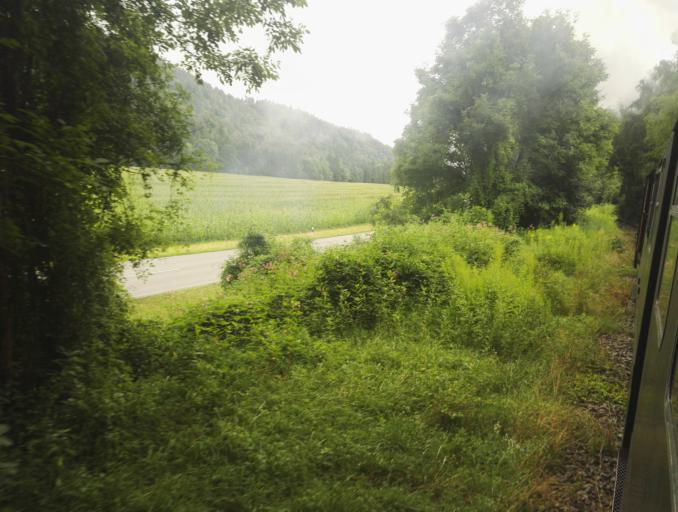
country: CH
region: Schaffhausen
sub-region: Bezirk Schleitheim
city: Schleitheim
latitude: 47.7756
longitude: 8.4864
